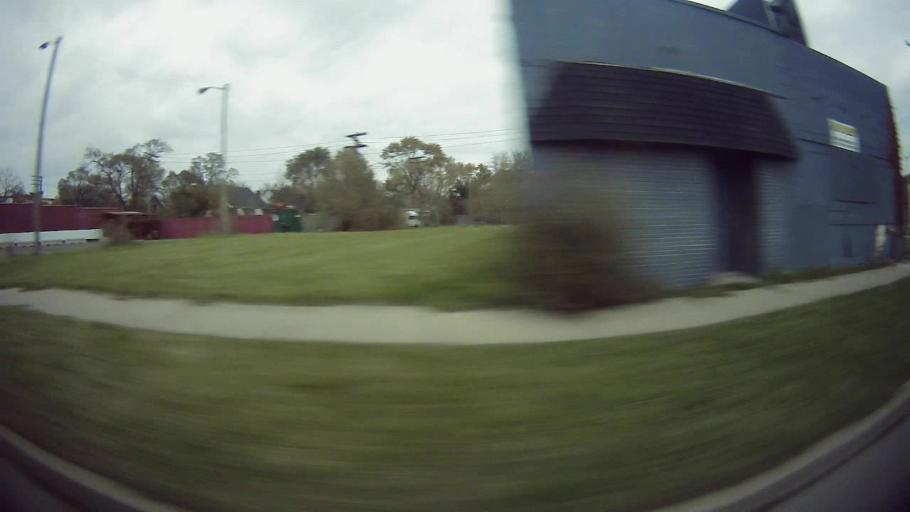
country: US
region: Michigan
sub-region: Wayne County
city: Hamtramck
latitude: 42.4104
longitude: -83.0045
